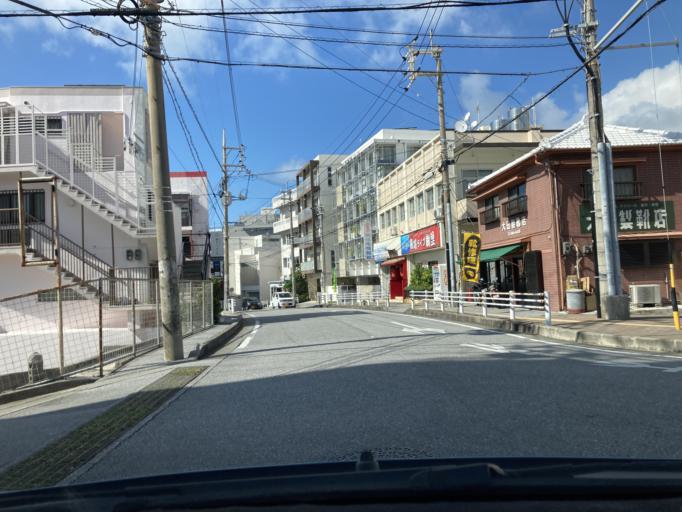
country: JP
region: Okinawa
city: Naha-shi
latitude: 26.2137
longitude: 127.6849
